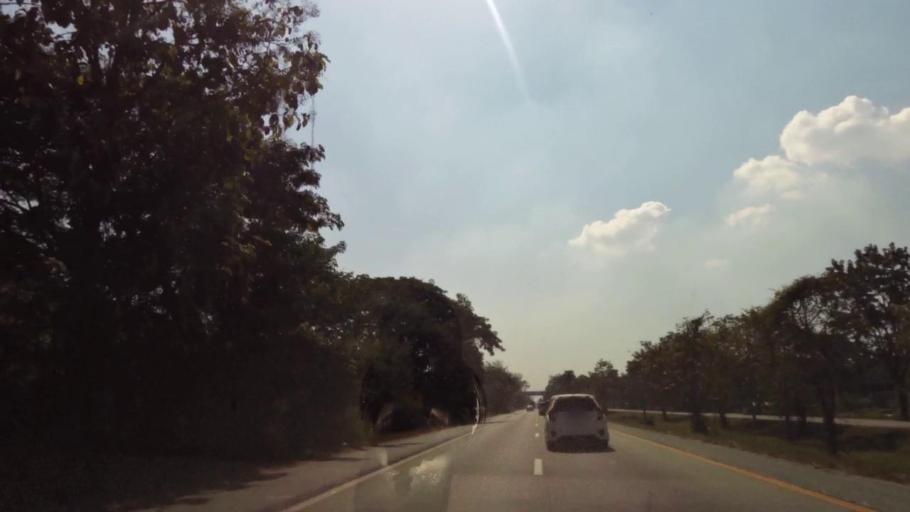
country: TH
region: Phichit
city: Wachira Barami
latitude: 16.5524
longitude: 100.1469
